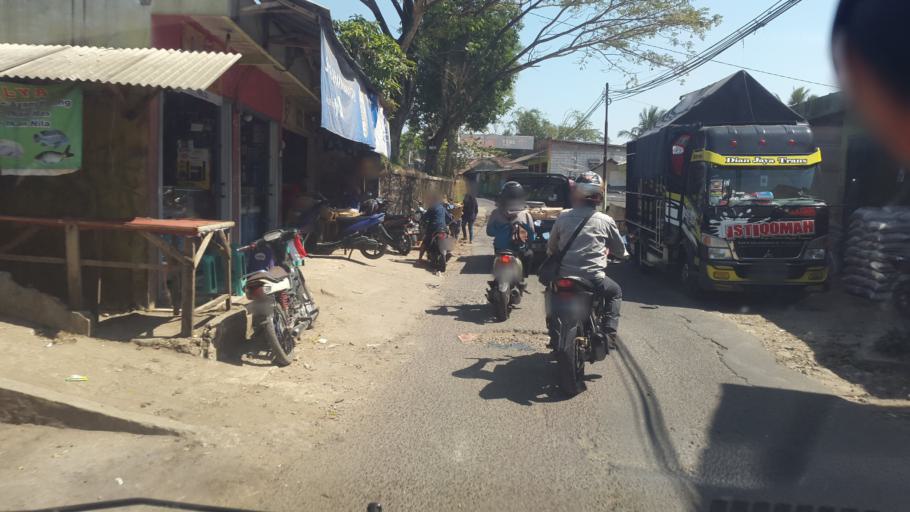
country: ID
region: West Java
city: Cicurug
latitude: -6.8336
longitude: 106.6675
